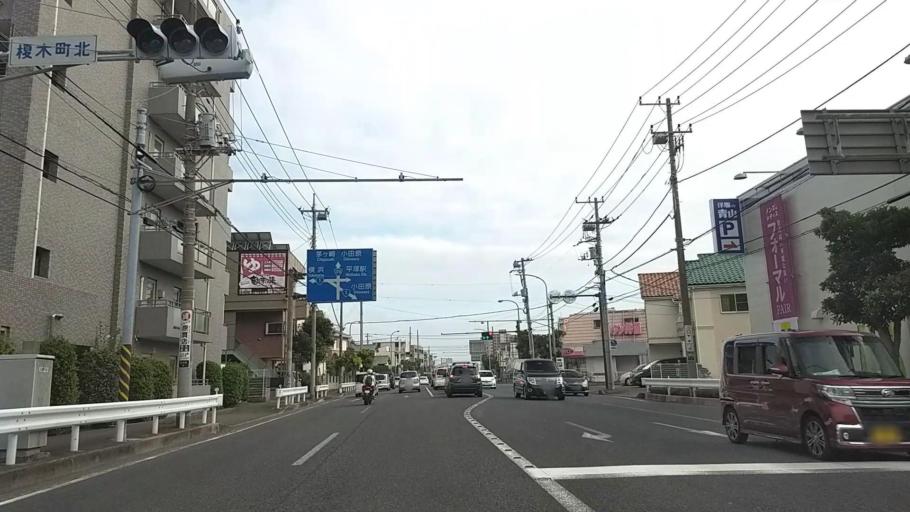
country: JP
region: Kanagawa
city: Hiratsuka
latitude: 35.3332
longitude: 139.3588
